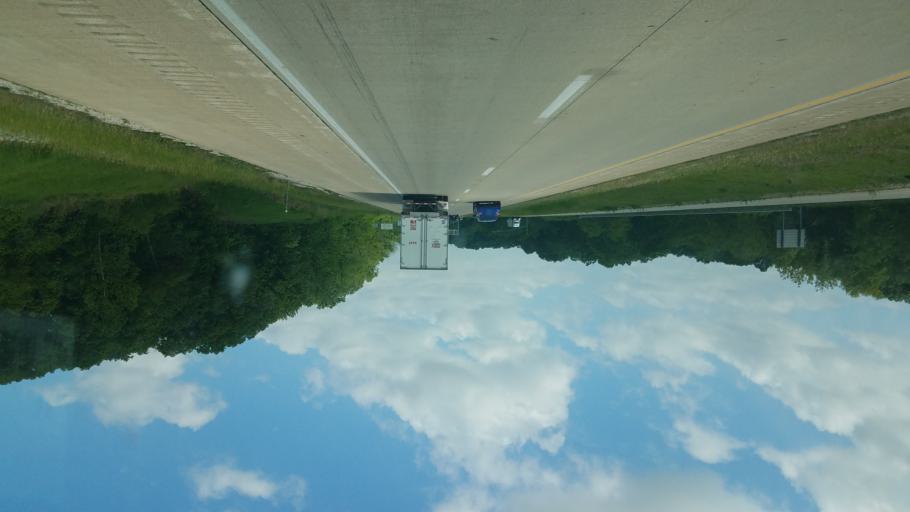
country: US
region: Indiana
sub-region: Vigo County
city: West Terre Haute
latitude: 39.4328
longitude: -87.5407
